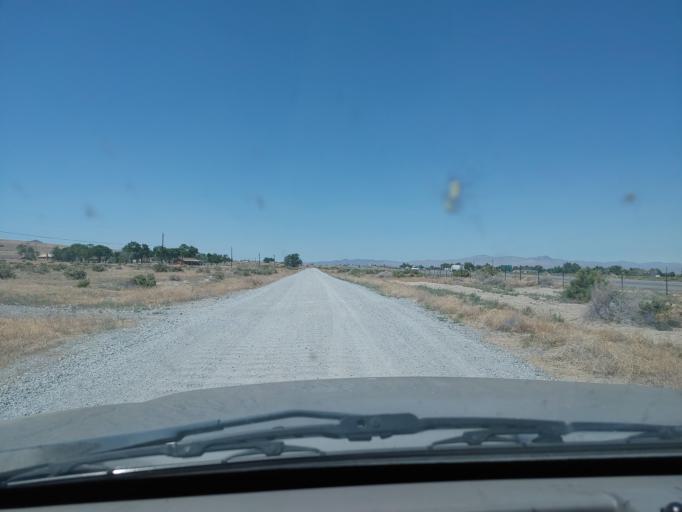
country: US
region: Nevada
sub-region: Humboldt County
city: Winnemucca
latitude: 40.6591
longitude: -118.1371
